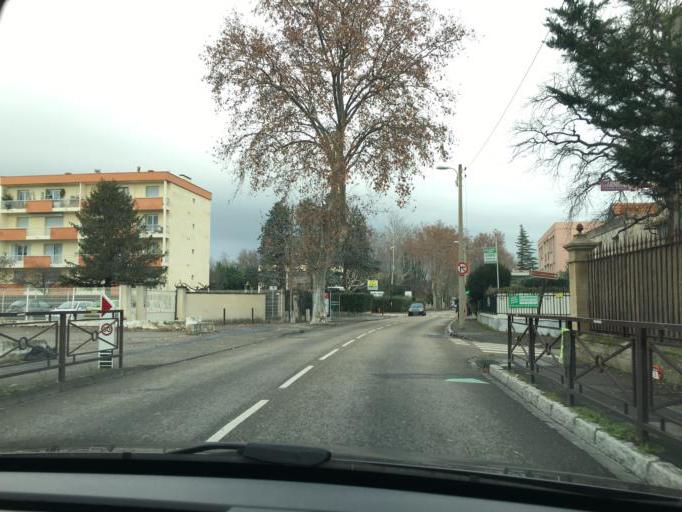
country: FR
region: Provence-Alpes-Cote d'Azur
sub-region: Departement du Vaucluse
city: Avignon
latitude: 43.9308
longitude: 4.8095
